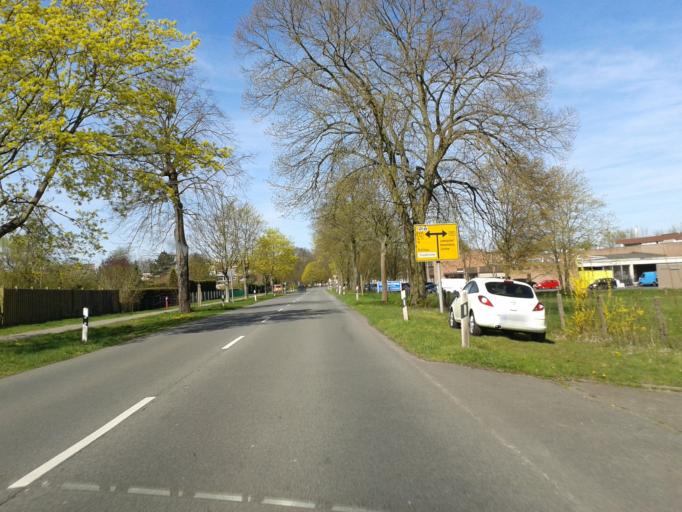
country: DE
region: Lower Saxony
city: Uelzen
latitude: 52.9623
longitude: 10.5827
